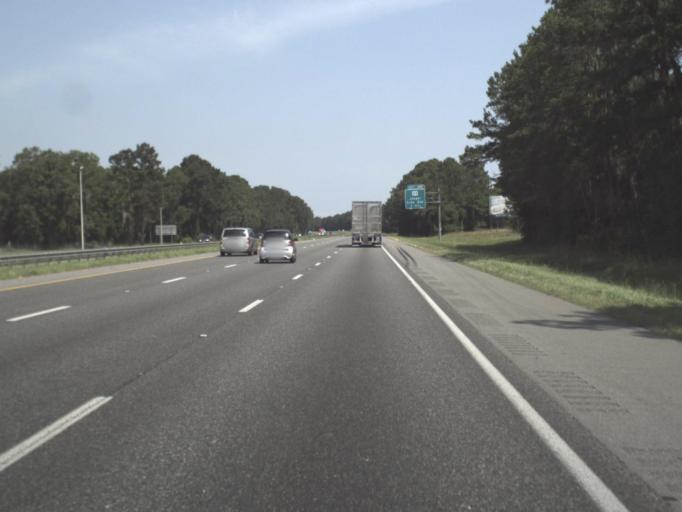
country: US
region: Florida
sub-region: Hamilton County
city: Jasper
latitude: 30.4293
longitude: -82.9083
